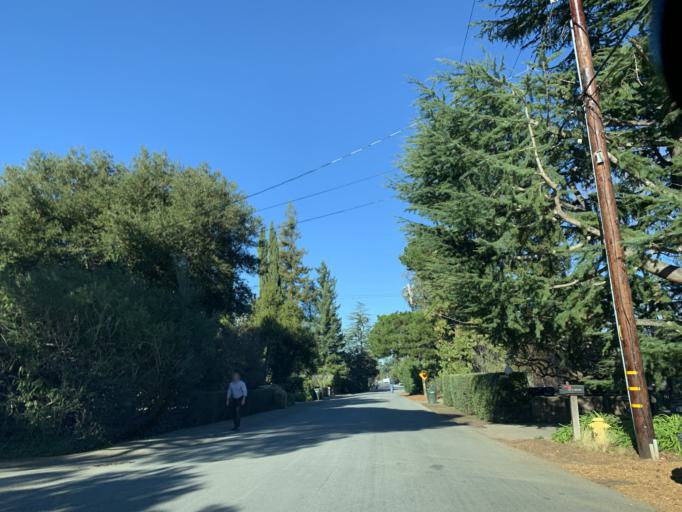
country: US
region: California
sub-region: Santa Clara County
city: Los Altos
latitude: 37.3804
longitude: -122.1074
